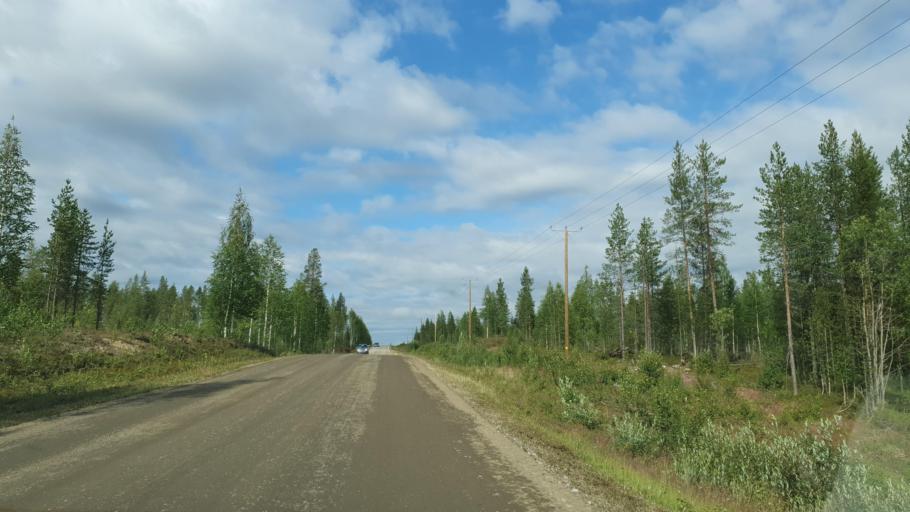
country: FI
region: Lapland
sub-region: Pohjois-Lappi
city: Sodankylae
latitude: 67.5364
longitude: 25.9658
